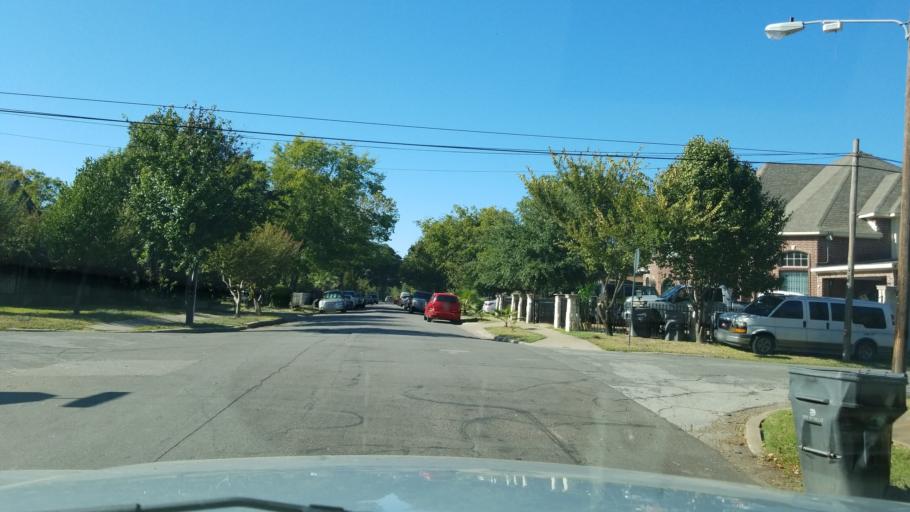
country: US
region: Texas
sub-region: Dallas County
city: Highland Park
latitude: 32.7994
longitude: -96.7444
